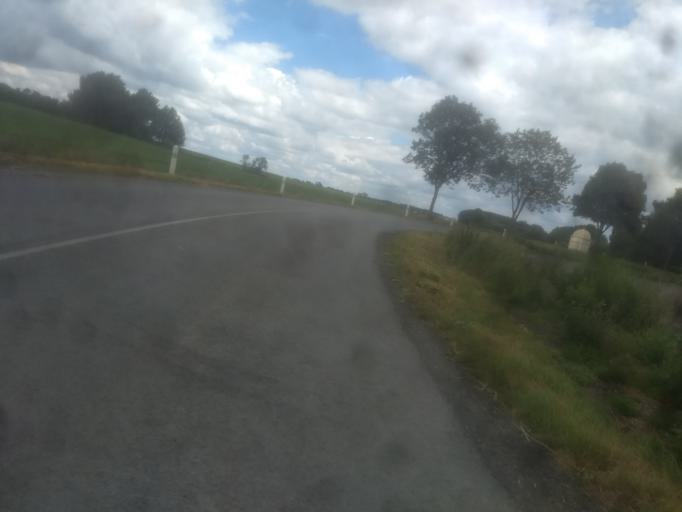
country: FR
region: Nord-Pas-de-Calais
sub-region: Departement du Pas-de-Calais
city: Beaurains
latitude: 50.2119
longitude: 2.7911
